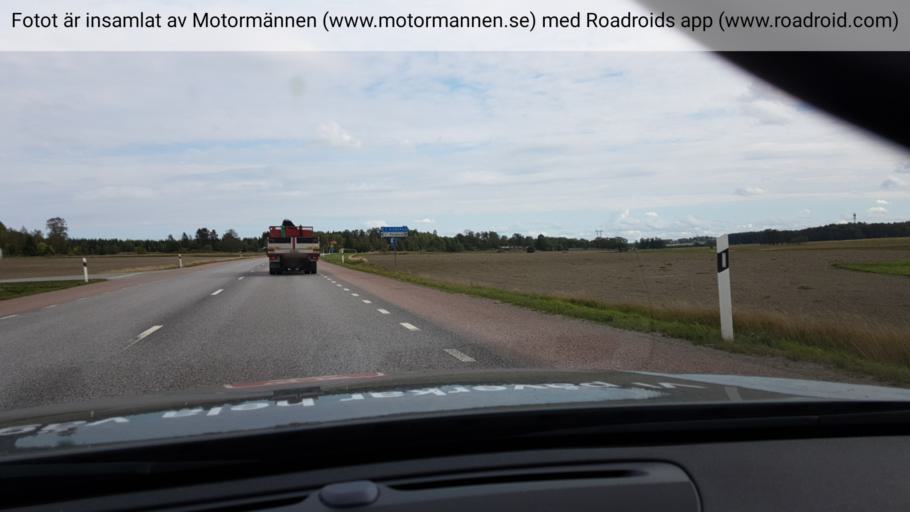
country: SE
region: Stockholm
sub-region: Sigtuna Kommun
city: Marsta
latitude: 59.7502
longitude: 17.9640
